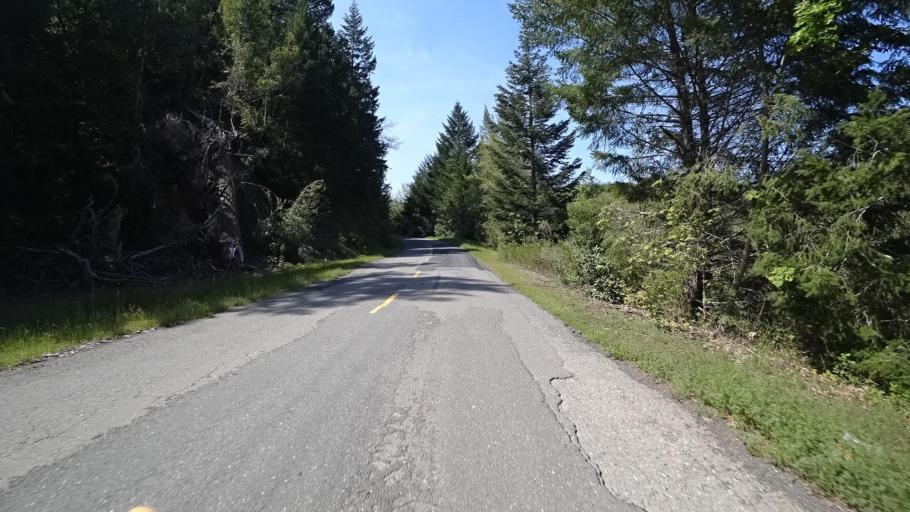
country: US
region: California
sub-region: Humboldt County
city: Redway
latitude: 40.3311
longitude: -123.6711
